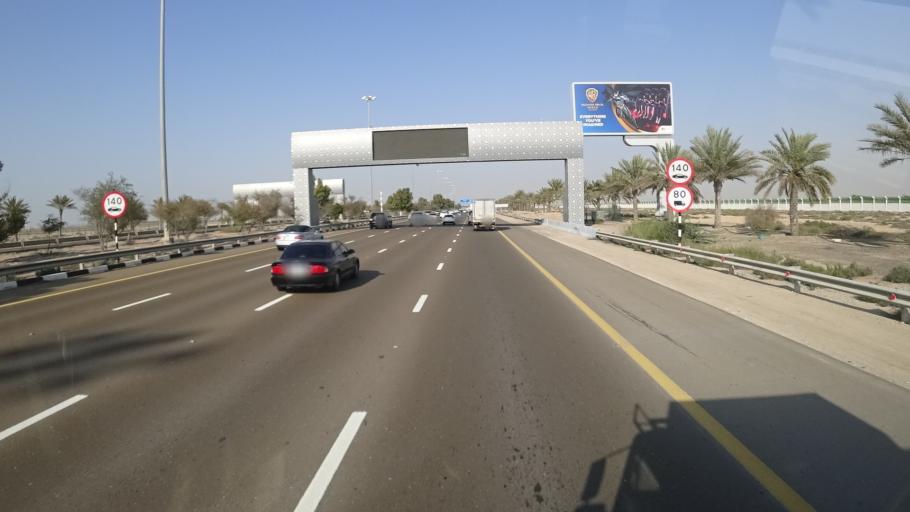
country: AE
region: Dubai
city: Dubai
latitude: 24.8760
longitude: 54.9234
